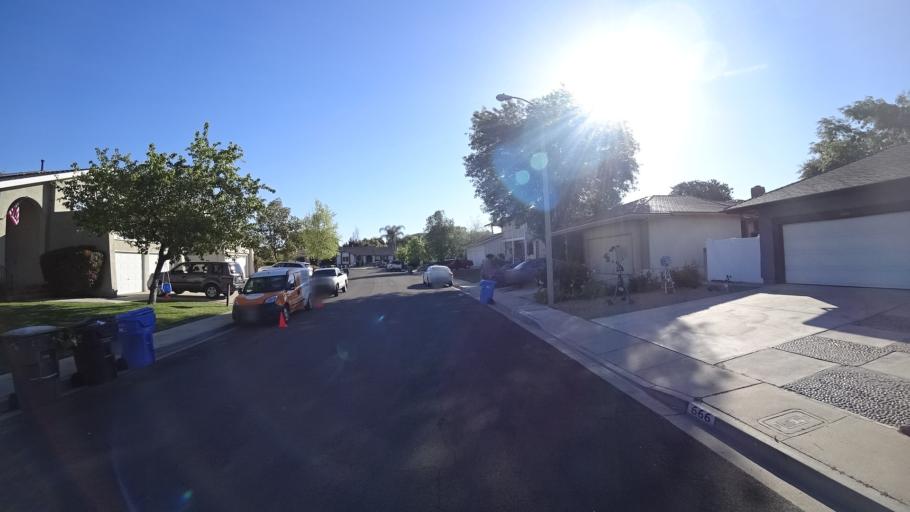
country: US
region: California
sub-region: Ventura County
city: Casa Conejo
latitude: 34.2163
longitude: -118.8955
